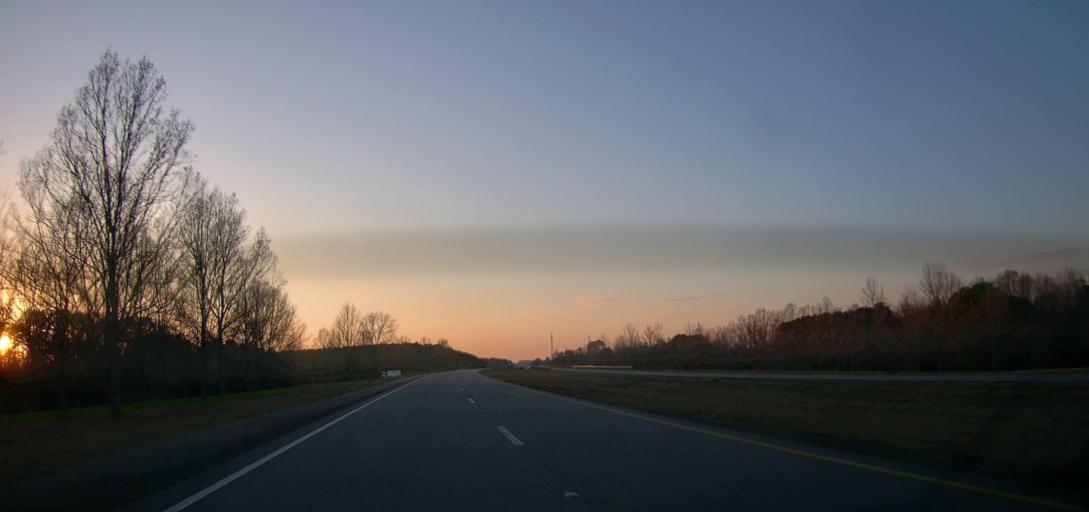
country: US
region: Alabama
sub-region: Coosa County
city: Goodwater
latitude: 32.9839
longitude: -86.0641
